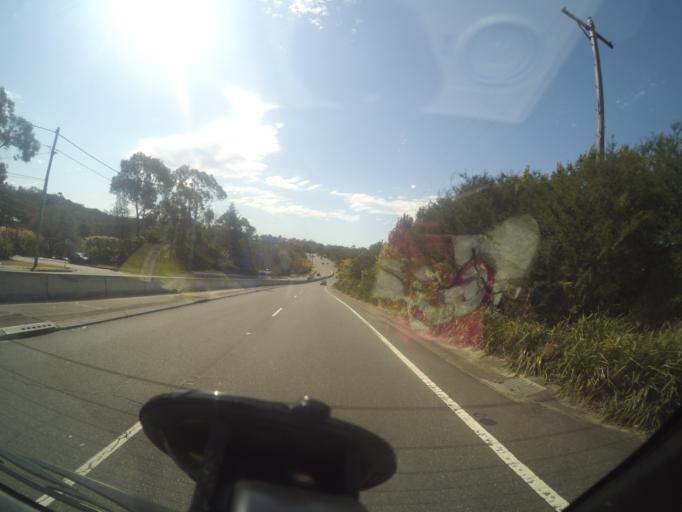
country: AU
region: New South Wales
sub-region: Blue Mountains Municipality
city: Hazelbrook
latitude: -33.7054
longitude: 150.5293
